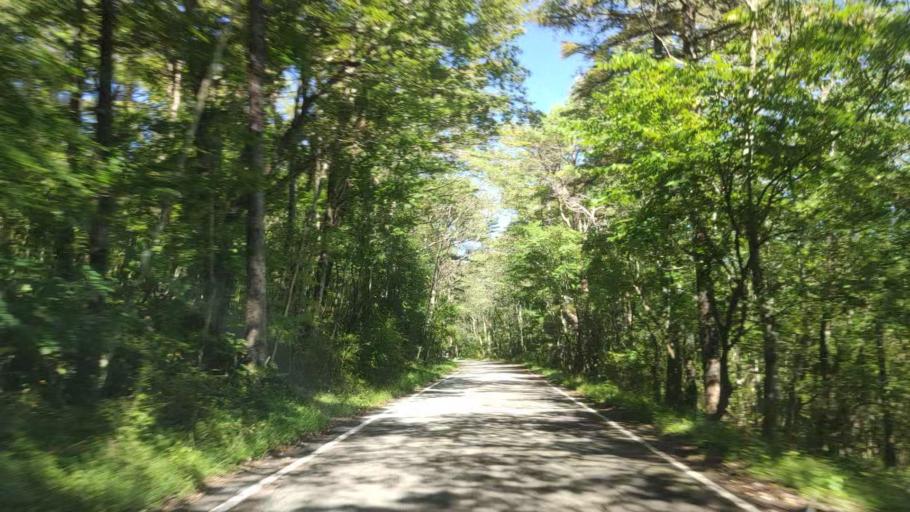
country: JP
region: Shizuoka
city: Gotemba
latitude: 35.4023
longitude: 138.8631
